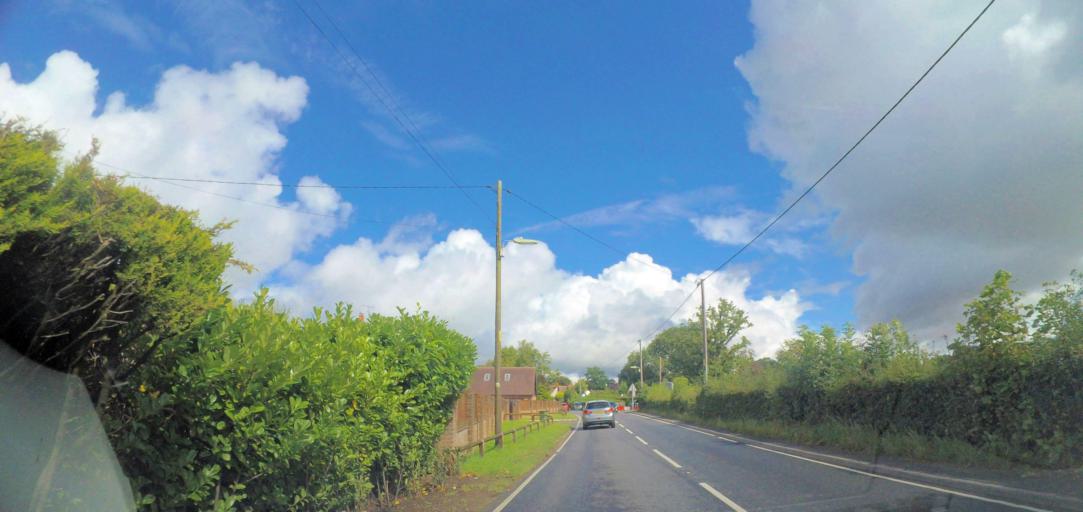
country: GB
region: England
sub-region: Hampshire
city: Colden Common
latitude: 50.9765
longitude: -1.3028
